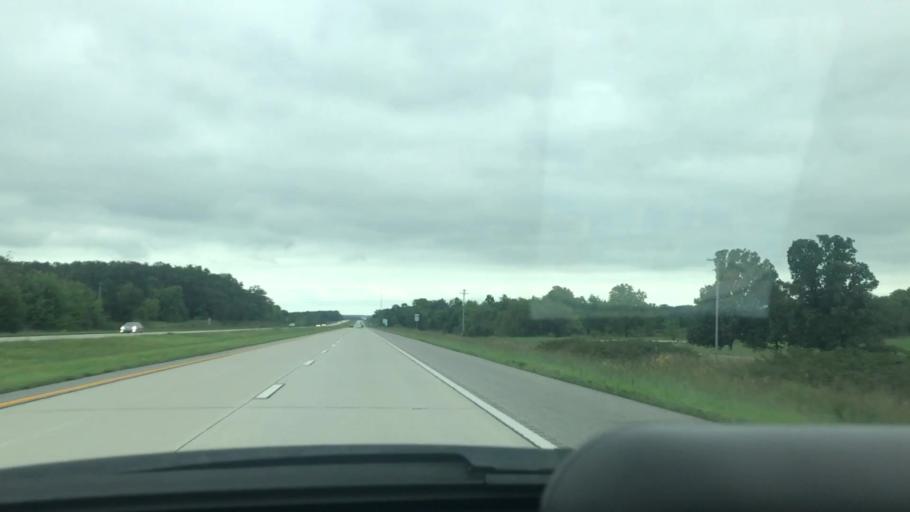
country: US
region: Missouri
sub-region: Greene County
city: Fair Grove
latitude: 37.4870
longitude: -93.1391
